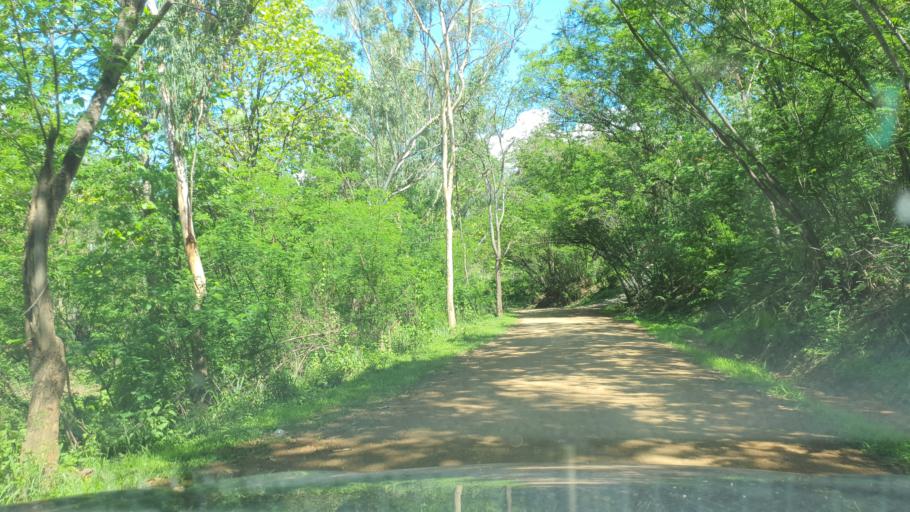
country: TH
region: Chiang Mai
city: Mae On
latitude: 18.8042
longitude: 99.2662
